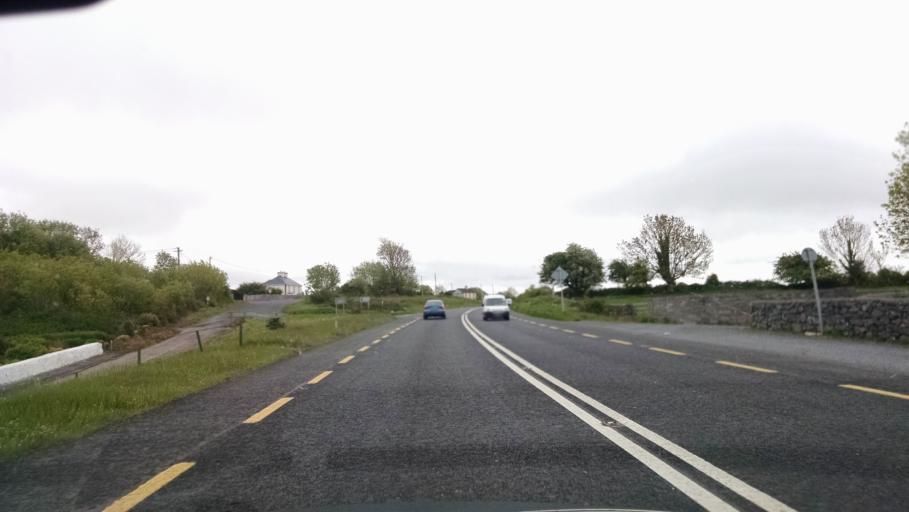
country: IE
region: Connaught
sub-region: County Galway
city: Claregalway
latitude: 53.4107
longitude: -9.0191
